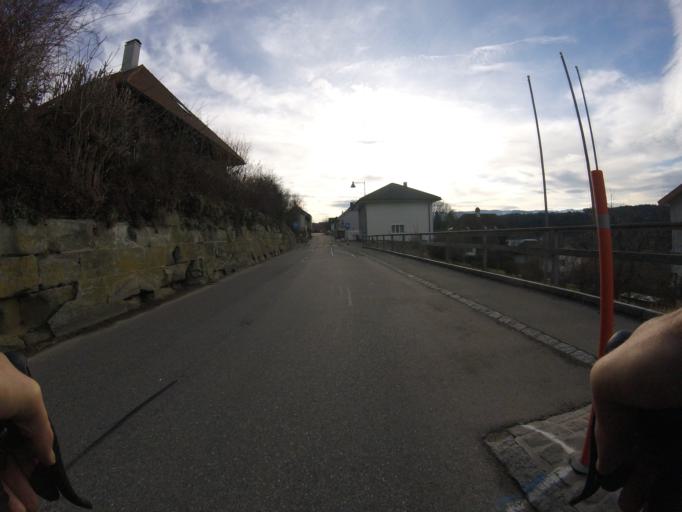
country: CH
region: Fribourg
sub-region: Sense District
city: Ueberstorf
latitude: 46.8529
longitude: 7.3165
